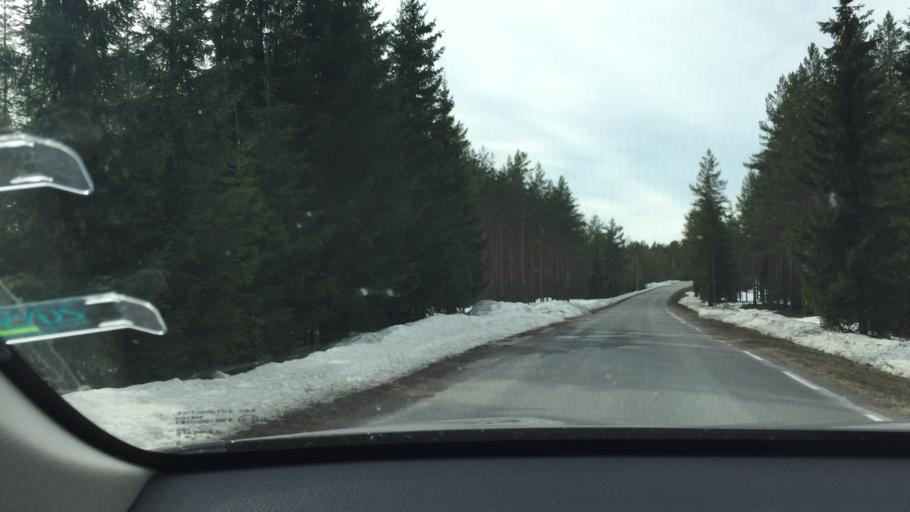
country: NO
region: Hedmark
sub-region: Trysil
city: Innbygda
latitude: 61.0640
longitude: 12.5980
